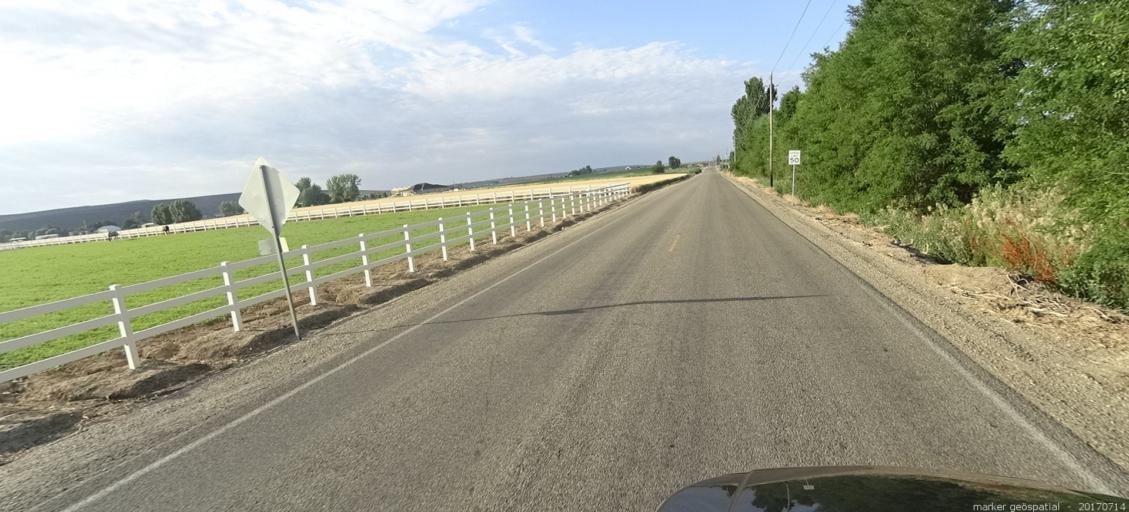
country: US
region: Idaho
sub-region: Ada County
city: Kuna
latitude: 43.4593
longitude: -116.4937
